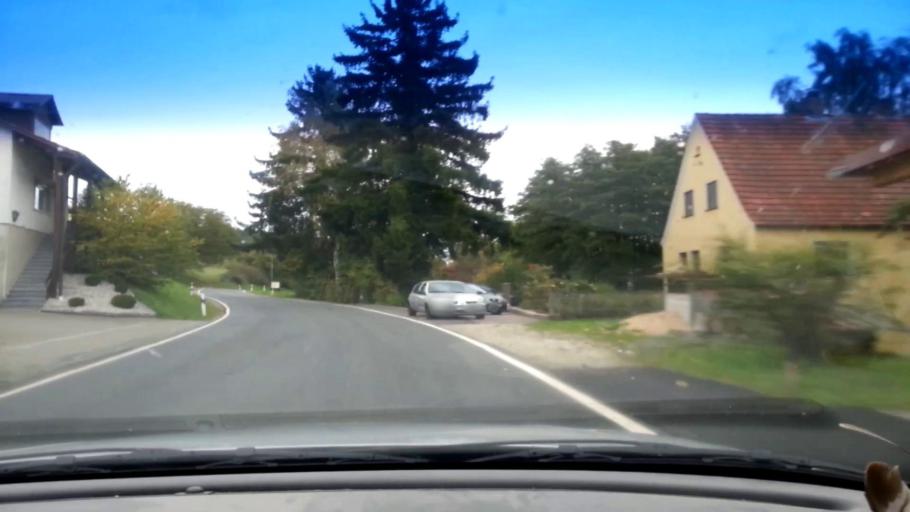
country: DE
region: Bavaria
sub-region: Upper Franconia
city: Lauter
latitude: 49.9806
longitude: 10.7712
